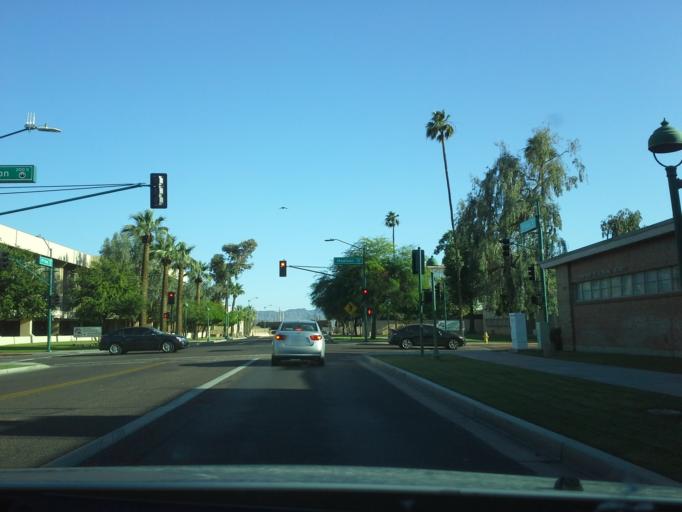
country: US
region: Arizona
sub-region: Maricopa County
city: Phoenix
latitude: 33.4464
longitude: -112.0959
